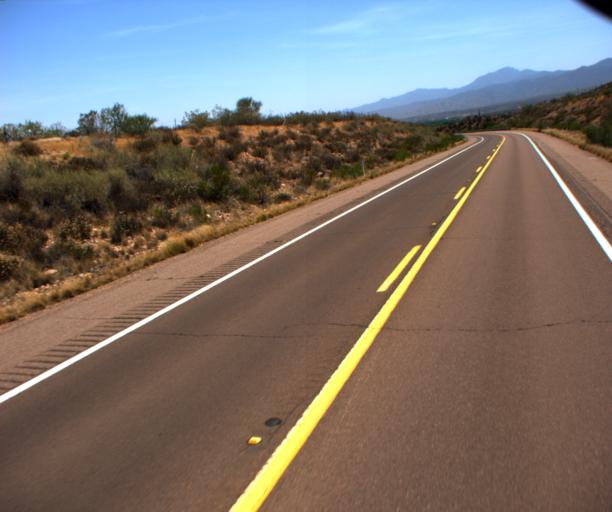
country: US
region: Arizona
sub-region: Gila County
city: Tonto Basin
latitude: 33.9012
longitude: -111.3106
